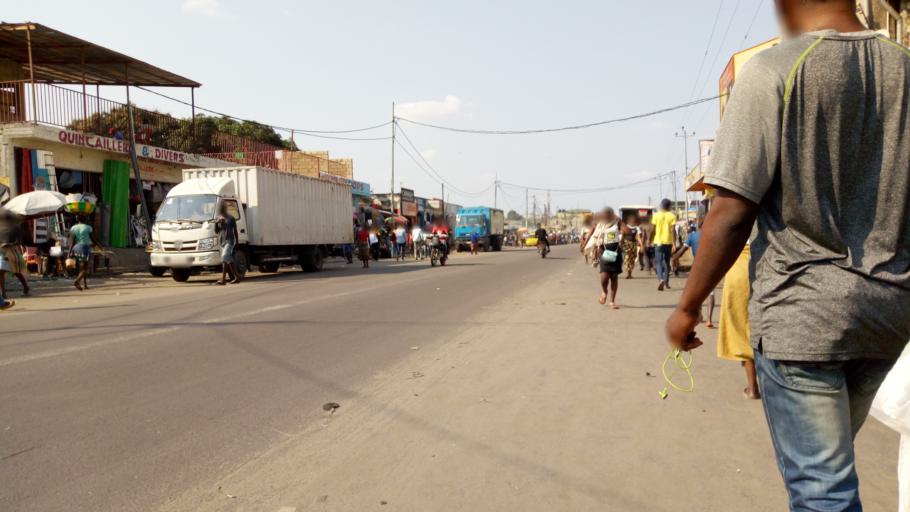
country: CD
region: Kinshasa
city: Kinshasa
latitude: -4.4500
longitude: 15.2475
